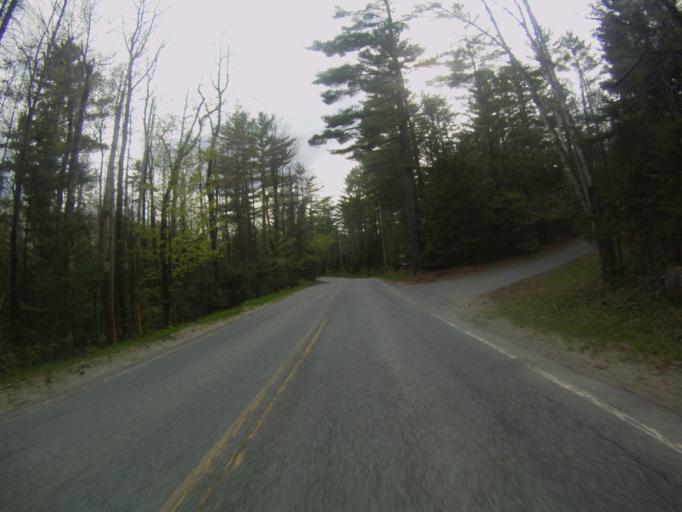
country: US
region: New York
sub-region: Warren County
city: Warrensburg
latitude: 43.8398
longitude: -73.8418
